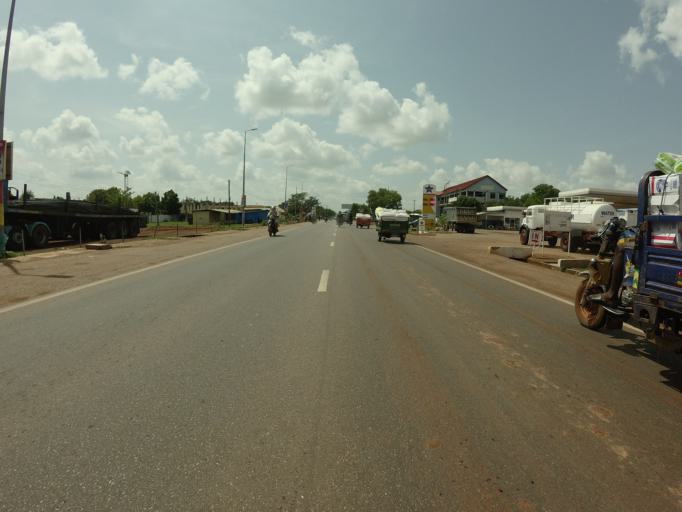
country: GH
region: Northern
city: Tamale
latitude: 9.4504
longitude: -0.8449
